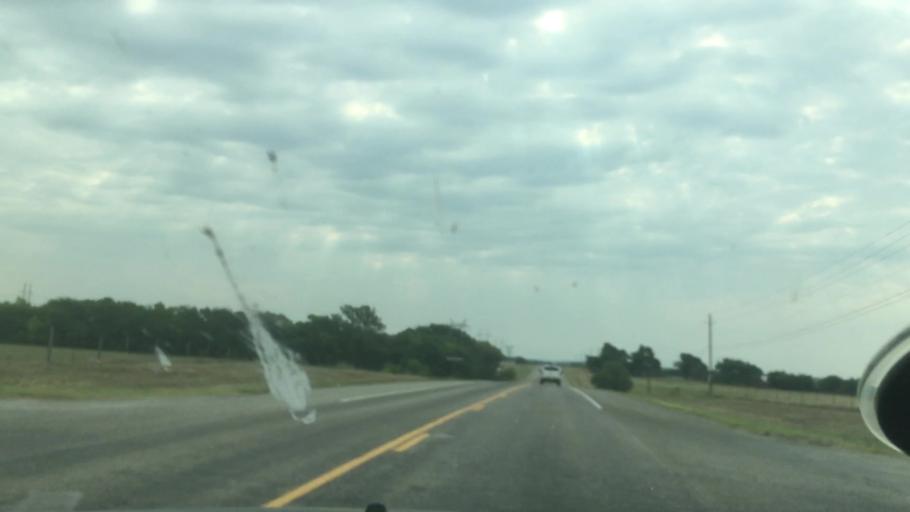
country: US
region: Texas
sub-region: Grayson County
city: Pottsboro
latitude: 33.7968
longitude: -96.6323
